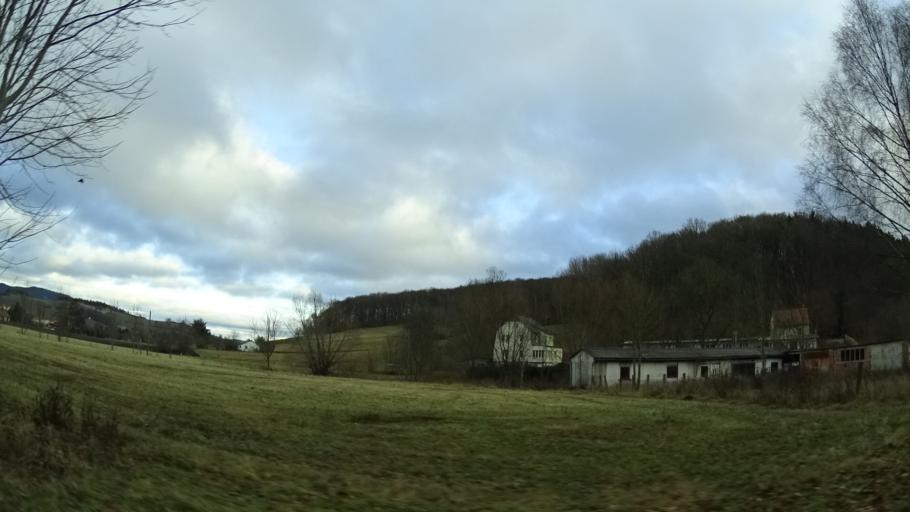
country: DE
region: Thuringia
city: Rittersdorf
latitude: 50.7548
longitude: 11.2185
